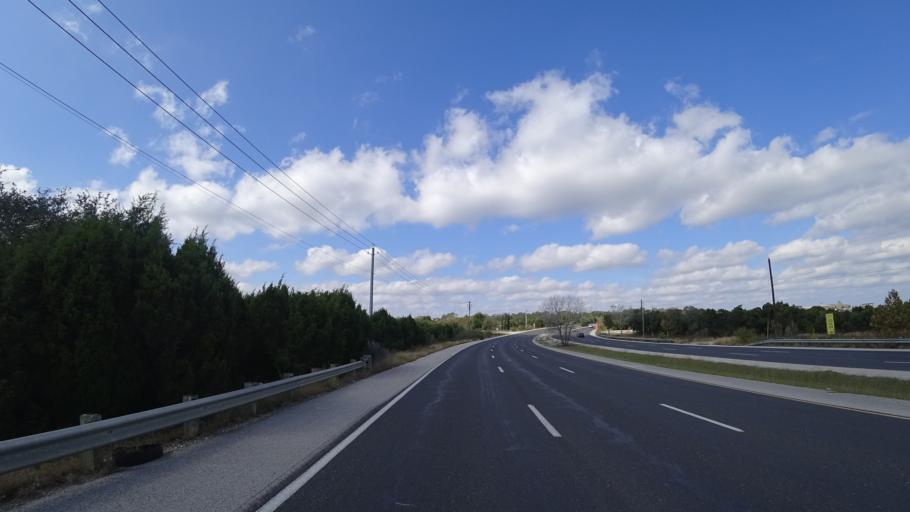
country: US
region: Texas
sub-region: Travis County
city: Barton Creek
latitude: 30.2568
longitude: -97.8805
